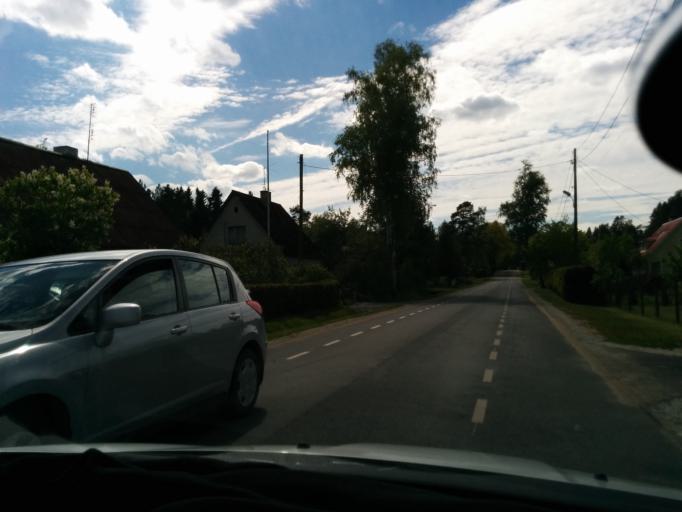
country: EE
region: Harju
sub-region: Loksa linn
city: Loksa
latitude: 59.5746
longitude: 25.7192
